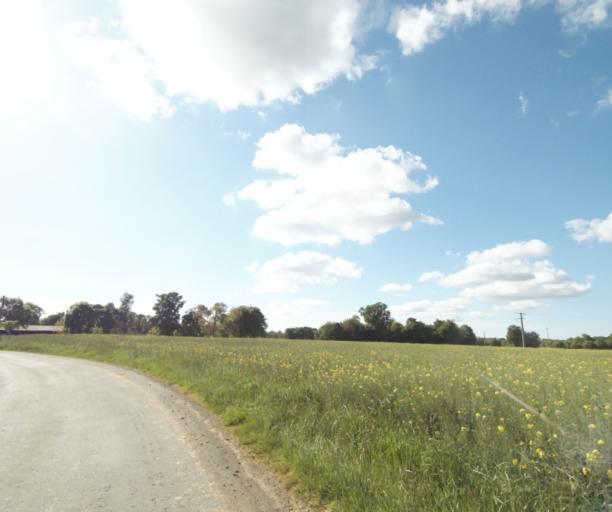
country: FR
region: Poitou-Charentes
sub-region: Departement de la Charente-Maritime
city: Nieul-les-Saintes
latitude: 45.7051
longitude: -0.7393
